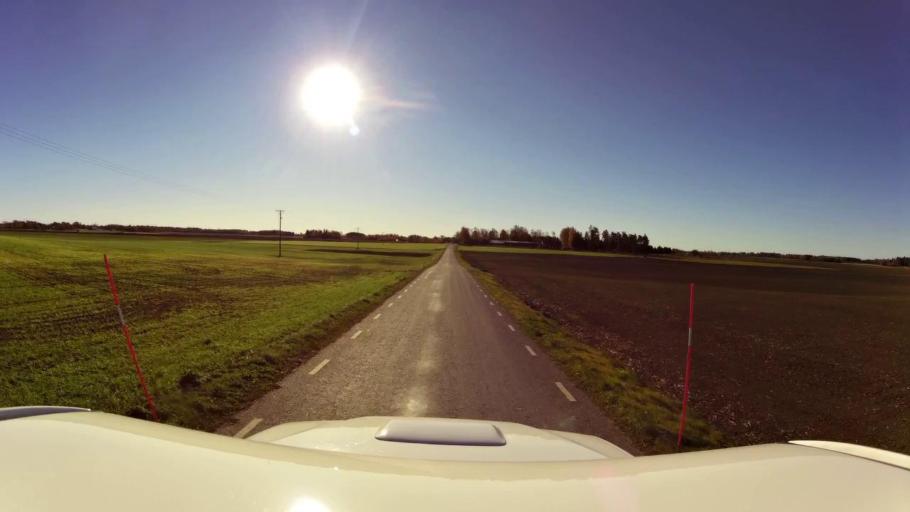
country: SE
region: OEstergoetland
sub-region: Linkopings Kommun
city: Ljungsbro
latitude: 58.5047
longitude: 15.4180
